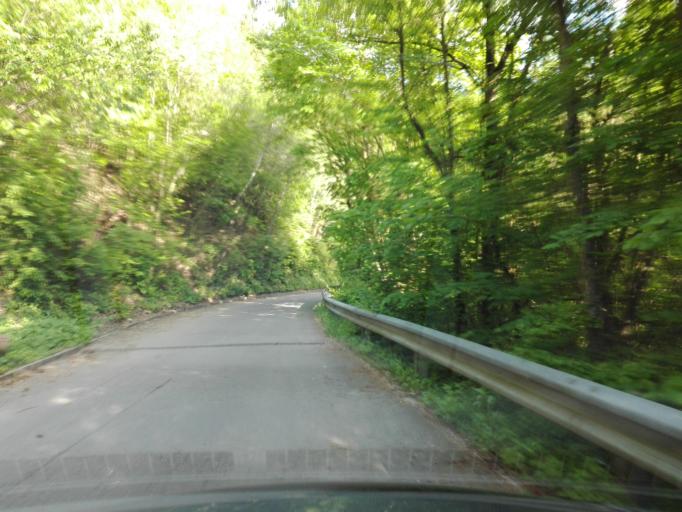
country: AT
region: Upper Austria
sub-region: Politischer Bezirk Rohrbach
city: Atzesberg
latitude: 48.4526
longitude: 13.9150
